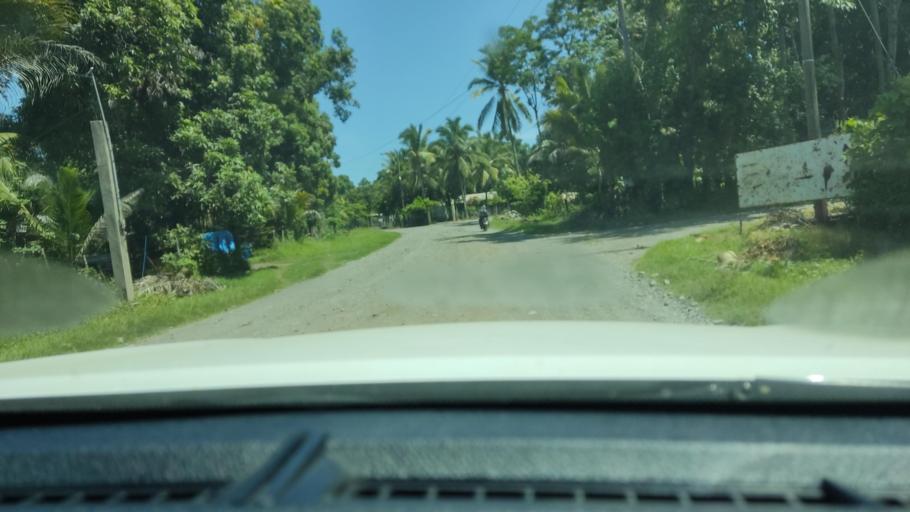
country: SV
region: Ahuachapan
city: San Francisco Menendez
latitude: 13.7523
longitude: -90.1209
